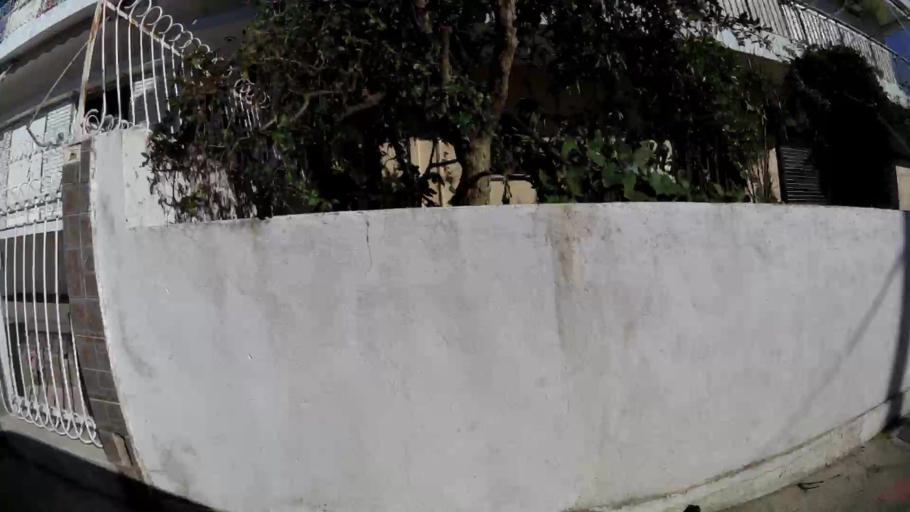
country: GR
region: Attica
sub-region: Nomarchia Anatolikis Attikis
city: Acharnes
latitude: 38.0941
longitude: 23.7194
